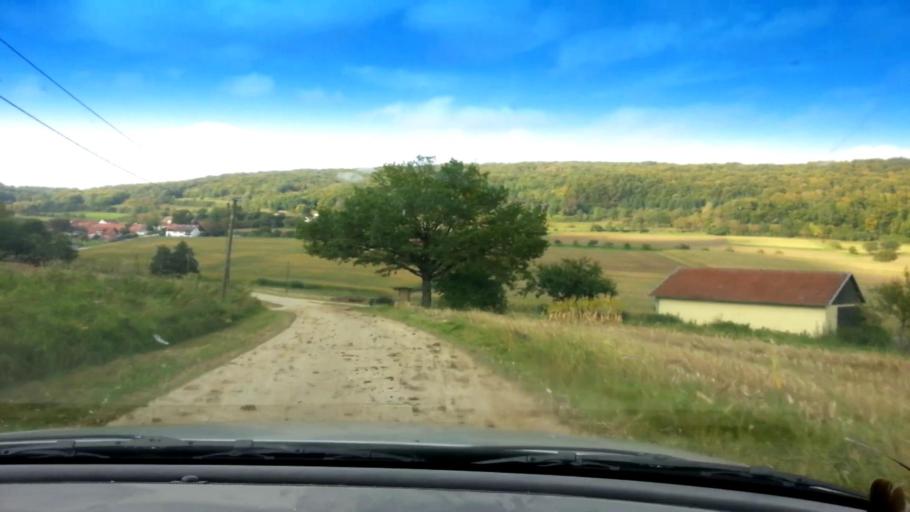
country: DE
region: Bavaria
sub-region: Upper Franconia
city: Schesslitz
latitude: 50.0061
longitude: 11.0481
